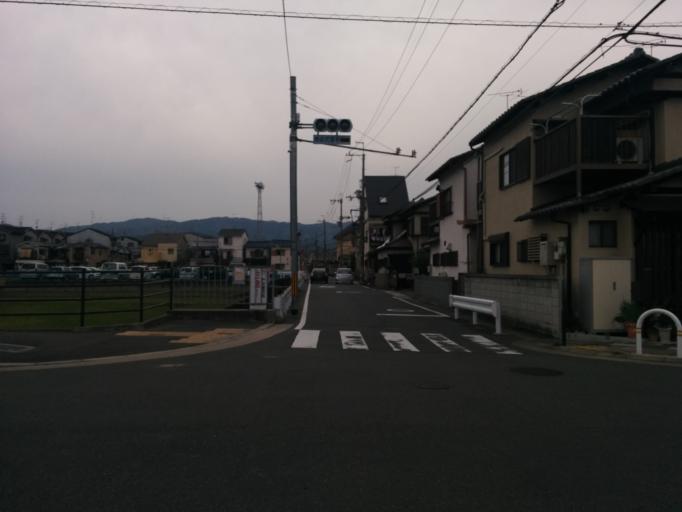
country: JP
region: Kyoto
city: Muko
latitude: 34.9399
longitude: 135.7121
